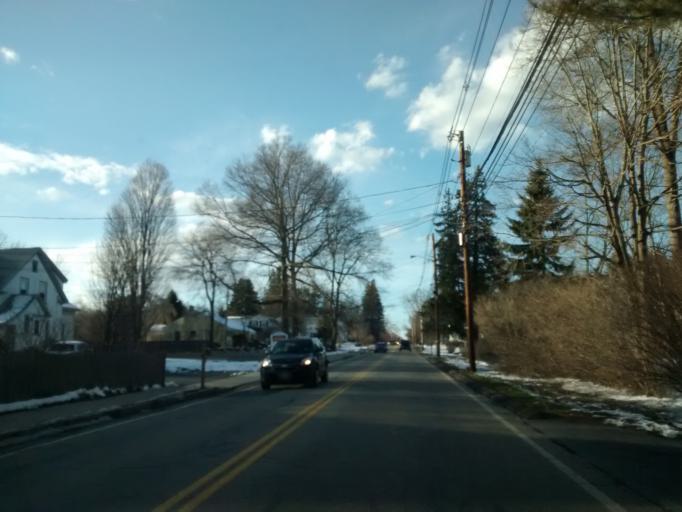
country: US
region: Massachusetts
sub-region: Middlesex County
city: Hopkinton
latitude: 42.2075
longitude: -71.5120
